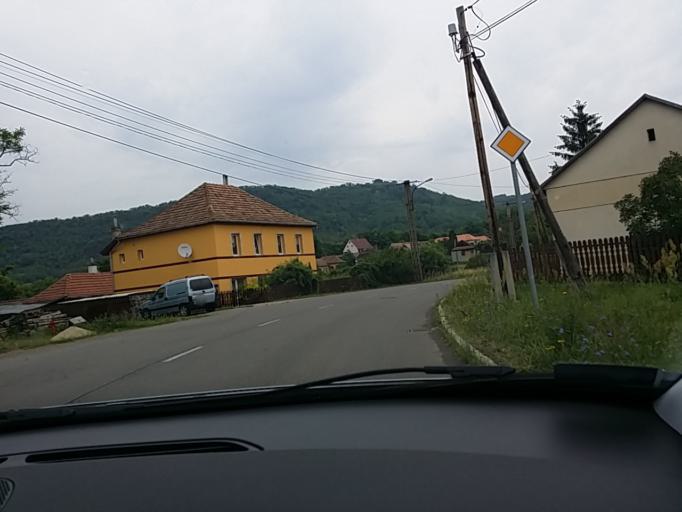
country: HU
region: Nograd
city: Kazar
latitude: 48.0059
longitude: 19.8946
